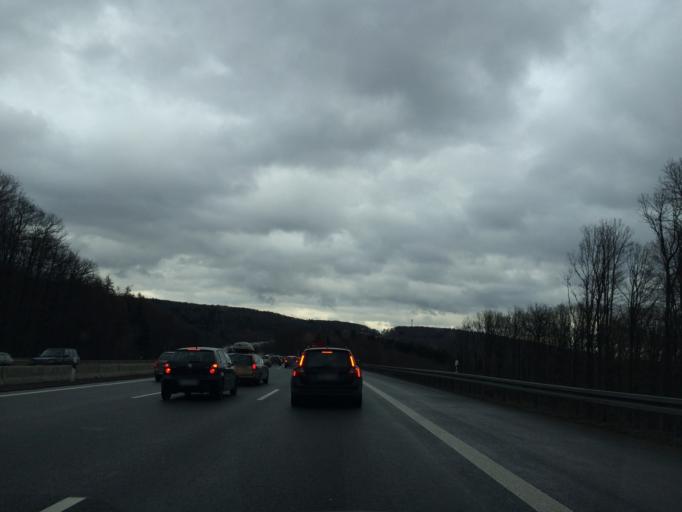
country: DE
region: Bavaria
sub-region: Regierungsbezirk Unterfranken
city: Altenbuch
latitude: 49.8825
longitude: 9.4245
